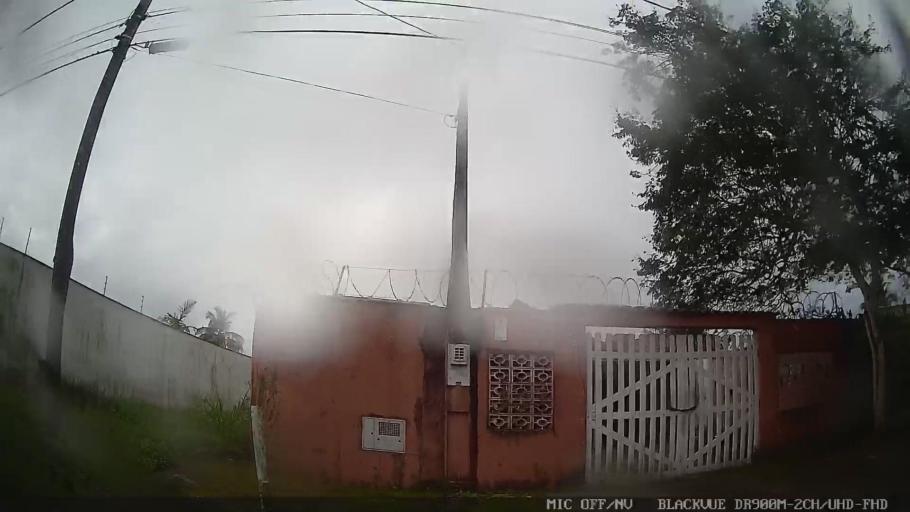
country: BR
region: Sao Paulo
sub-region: Itanhaem
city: Itanhaem
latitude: -24.2174
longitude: -46.8609
